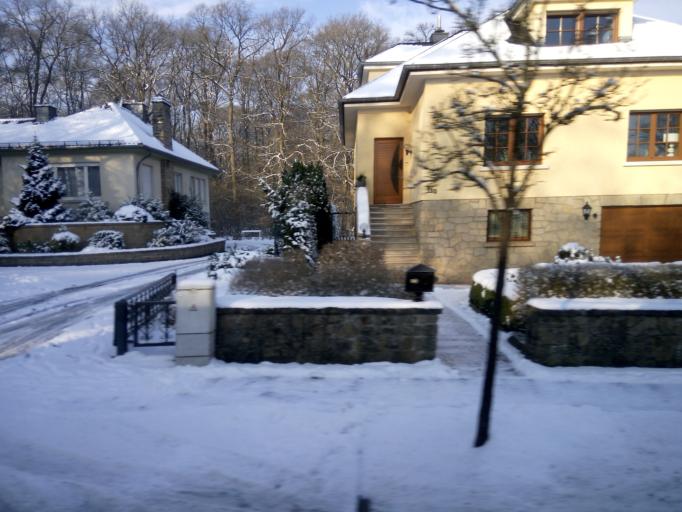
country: LU
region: Grevenmacher
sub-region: Canton d'Echternach
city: Consdorf
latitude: 49.7714
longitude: 6.3404
